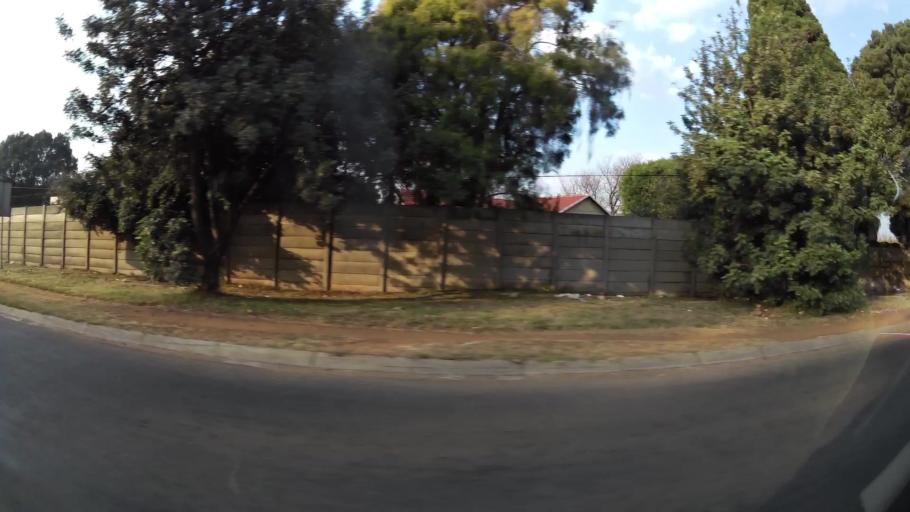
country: ZA
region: Gauteng
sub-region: Ekurhuleni Metropolitan Municipality
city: Benoni
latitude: -26.1376
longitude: 28.2936
